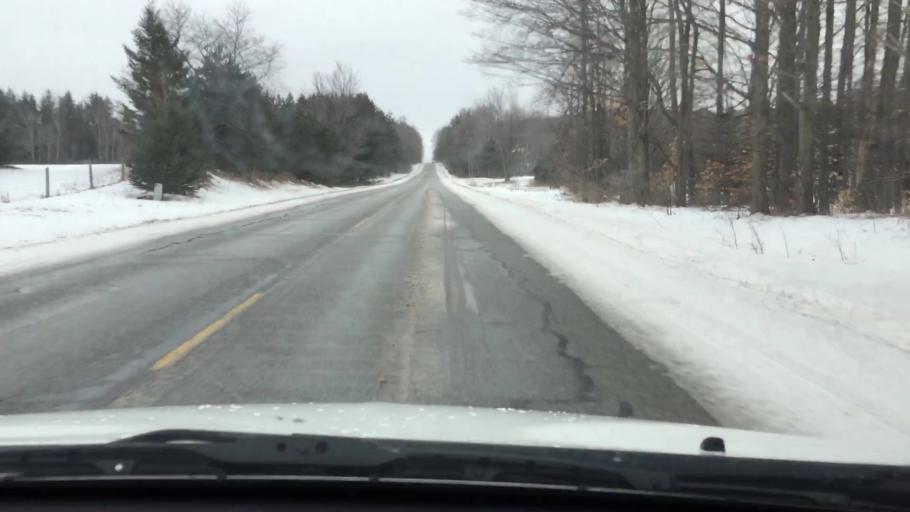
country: US
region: Michigan
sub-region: Wexford County
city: Cadillac
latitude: 44.1890
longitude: -85.4057
